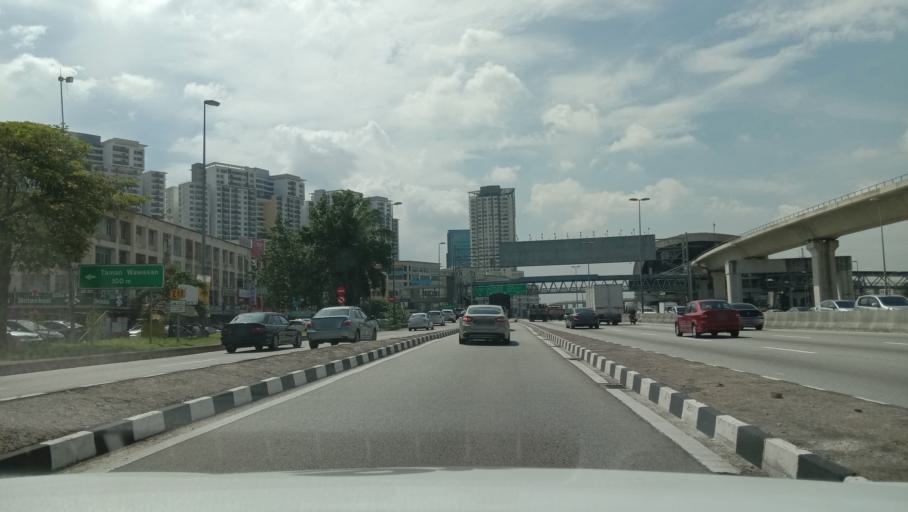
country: MY
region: Selangor
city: Subang Jaya
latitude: 3.0353
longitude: 101.6172
